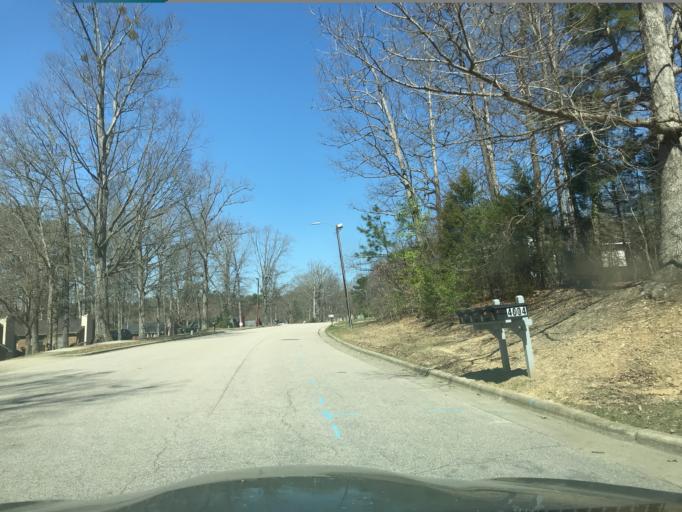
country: US
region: North Carolina
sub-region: Wake County
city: Raleigh
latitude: 35.8427
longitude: -78.5970
